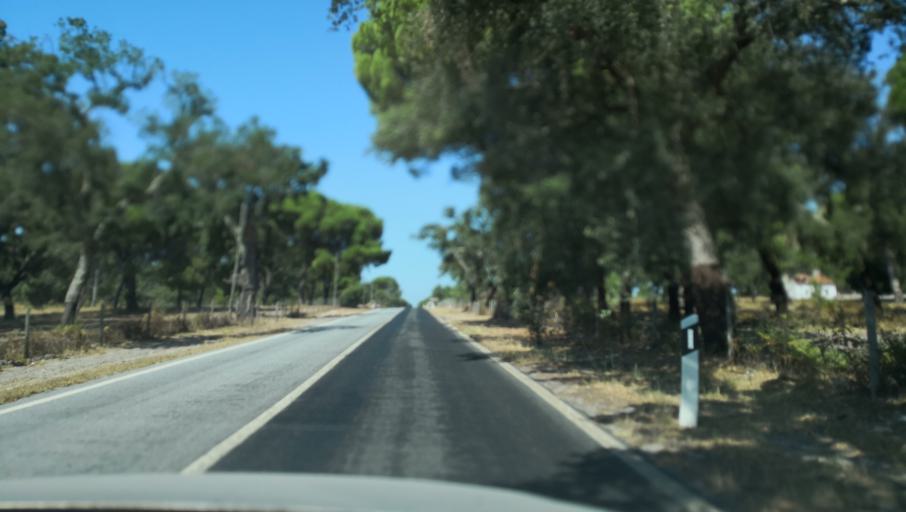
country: PT
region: Setubal
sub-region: Alcacer do Sal
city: Alcacer do Sal
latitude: 38.3741
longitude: -8.5525
